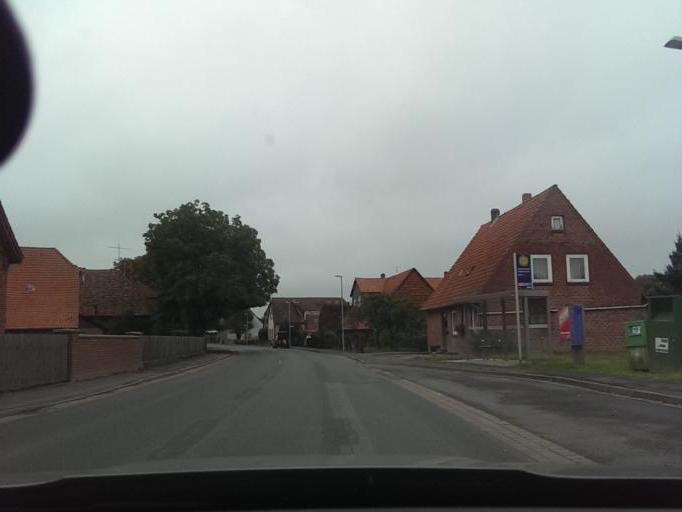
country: DE
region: Lower Saxony
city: Gross Munzel
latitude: 52.3679
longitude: 9.5050
